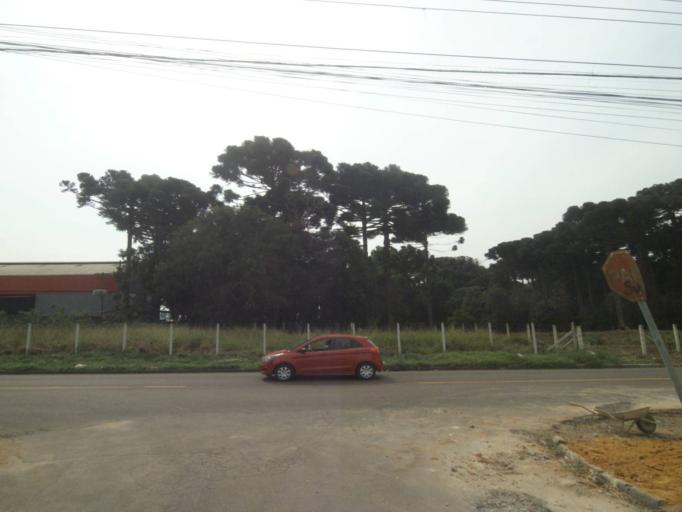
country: BR
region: Parana
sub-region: Sao Jose Dos Pinhais
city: Sao Jose dos Pinhais
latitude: -25.5276
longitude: -49.2802
